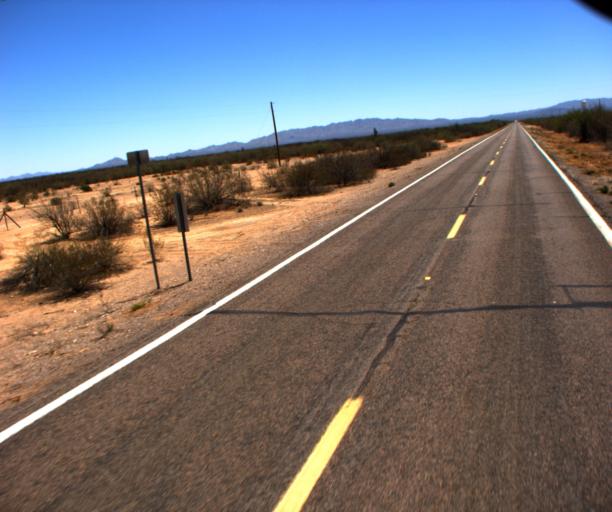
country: US
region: Arizona
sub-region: Pima County
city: Ajo
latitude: 32.1945
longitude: -112.4472
